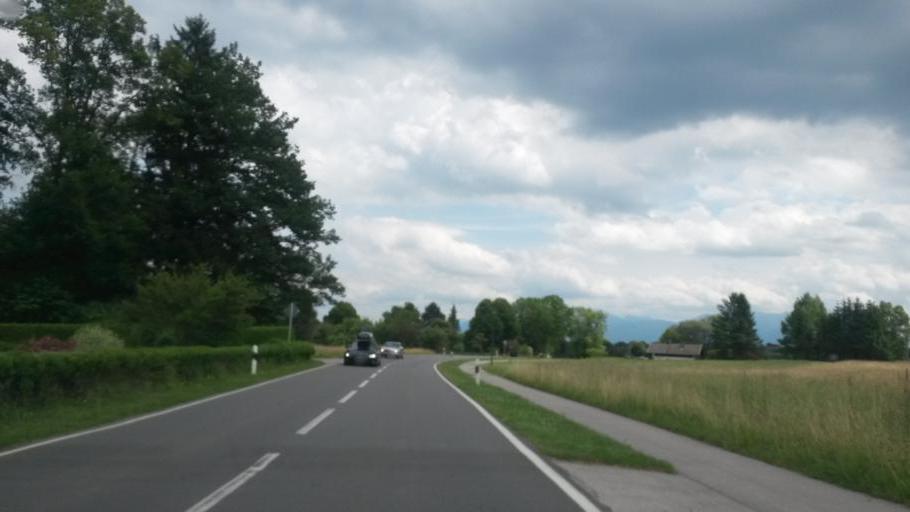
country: DE
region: Bavaria
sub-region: Upper Bavaria
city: Gstadt am Chiemsee
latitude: 47.8955
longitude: 12.3948
